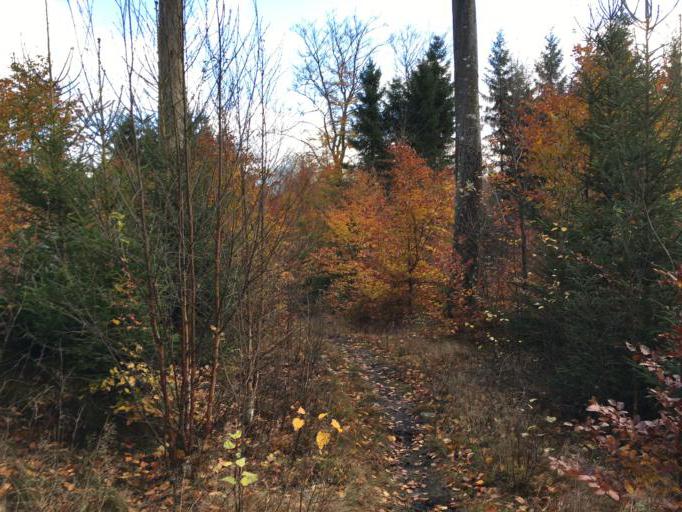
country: SE
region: Skane
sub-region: Hoors Kommun
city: Hoeoer
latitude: 55.9893
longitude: 13.5470
